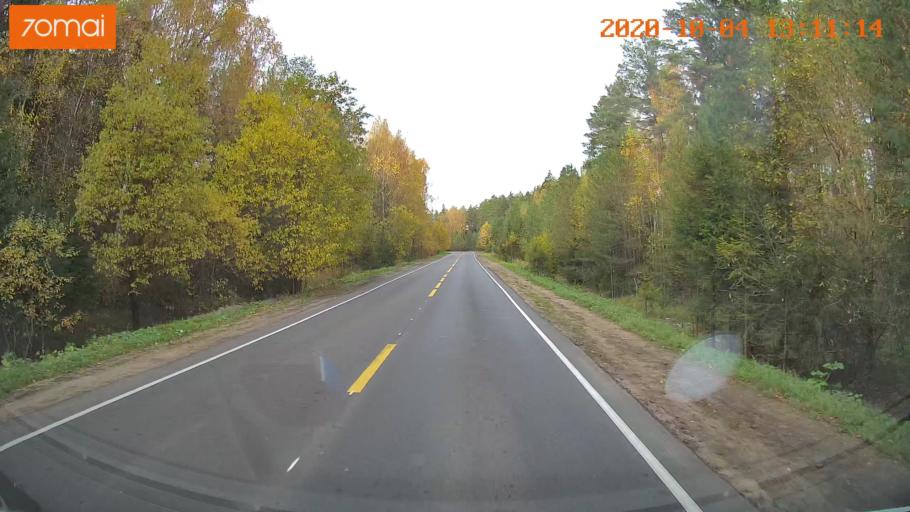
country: RU
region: Ivanovo
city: Bogorodskoye
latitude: 57.0753
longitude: 40.9472
